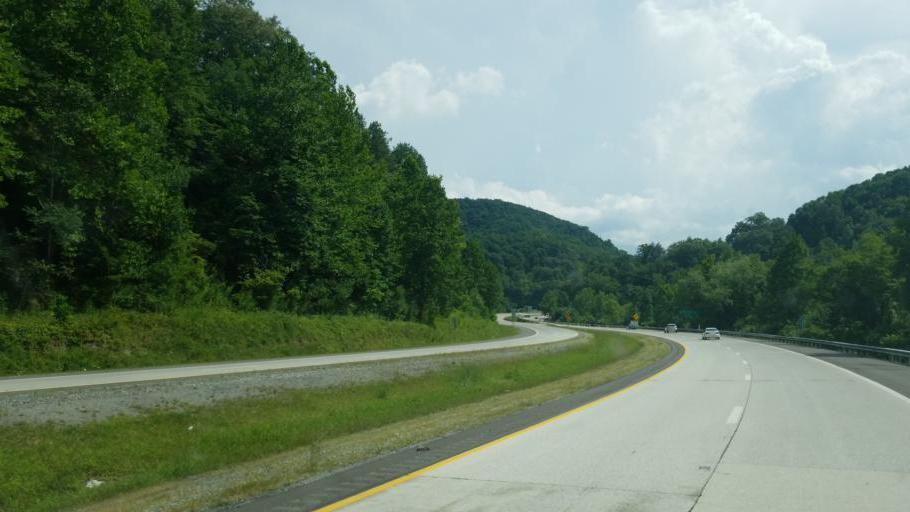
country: US
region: West Virginia
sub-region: Kanawha County
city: Alum Creek
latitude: 38.1856
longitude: -81.8504
